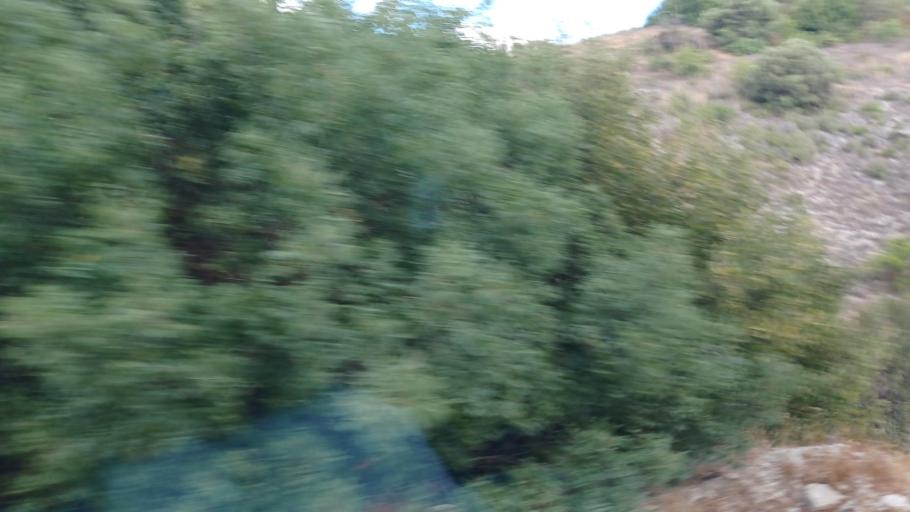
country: CY
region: Limassol
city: Pachna
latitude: 34.8081
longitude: 32.6756
